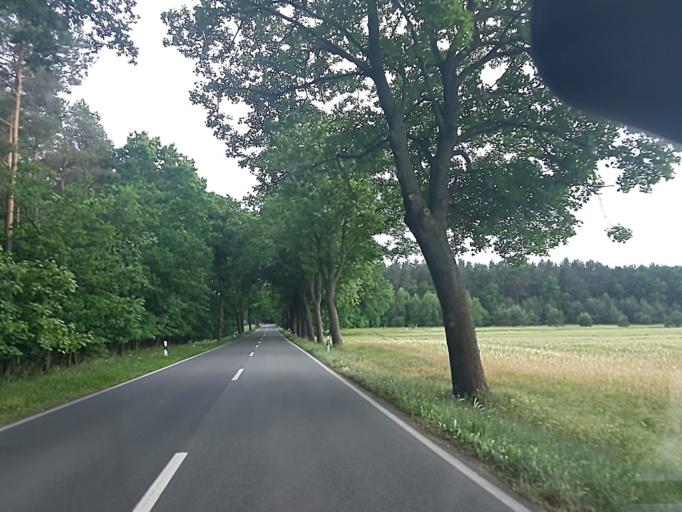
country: DE
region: Saxony-Anhalt
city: Nudersdorf
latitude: 51.9256
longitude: 12.6045
